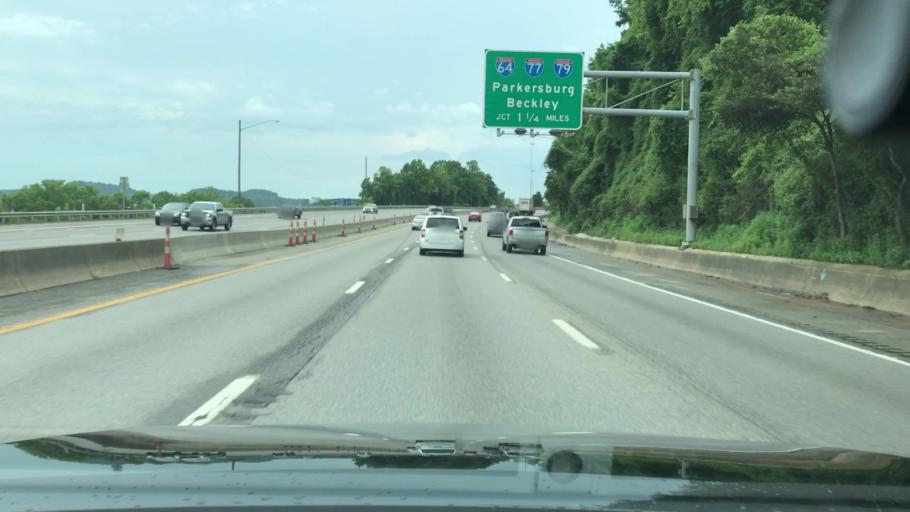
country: US
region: West Virginia
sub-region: Kanawha County
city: Charleston
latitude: 38.3571
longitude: -81.6574
